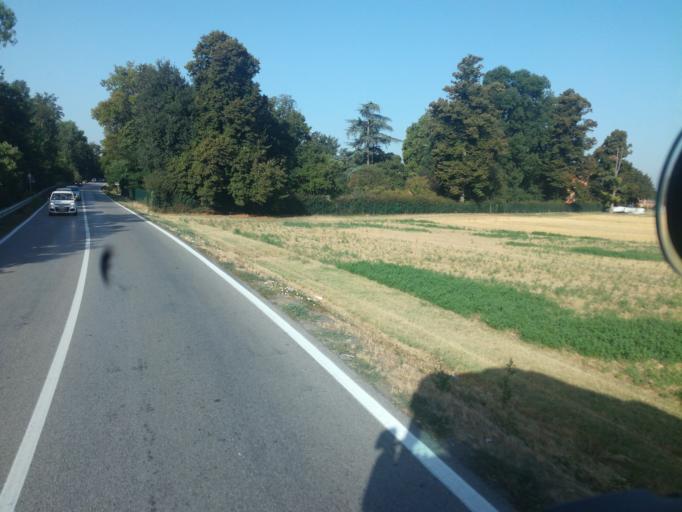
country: IT
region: Emilia-Romagna
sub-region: Provincia di Bologna
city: Progresso
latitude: 44.5502
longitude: 11.3849
